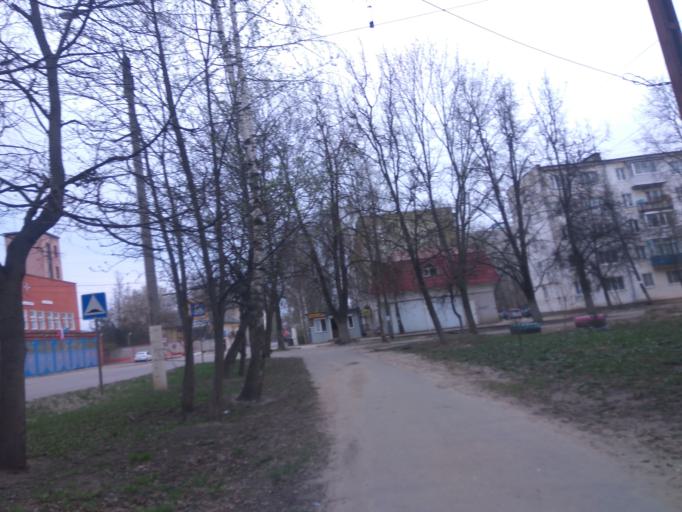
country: RU
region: Vladimir
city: Aleksandrov
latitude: 56.3991
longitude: 38.7136
